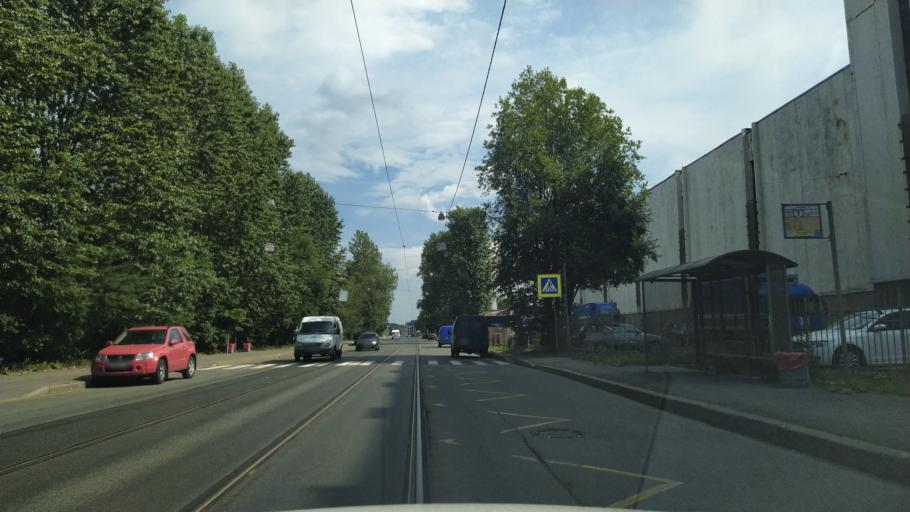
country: RU
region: Leningrad
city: Finlyandskiy
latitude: 59.9654
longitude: 30.3918
